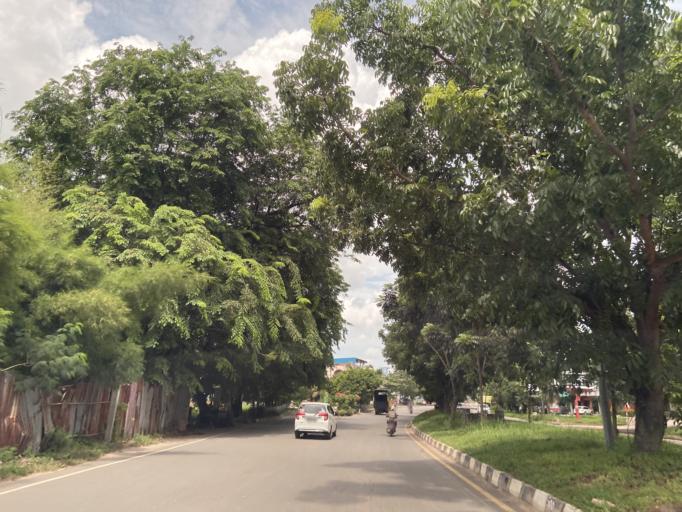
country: SG
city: Singapore
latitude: 1.1497
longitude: 104.0033
